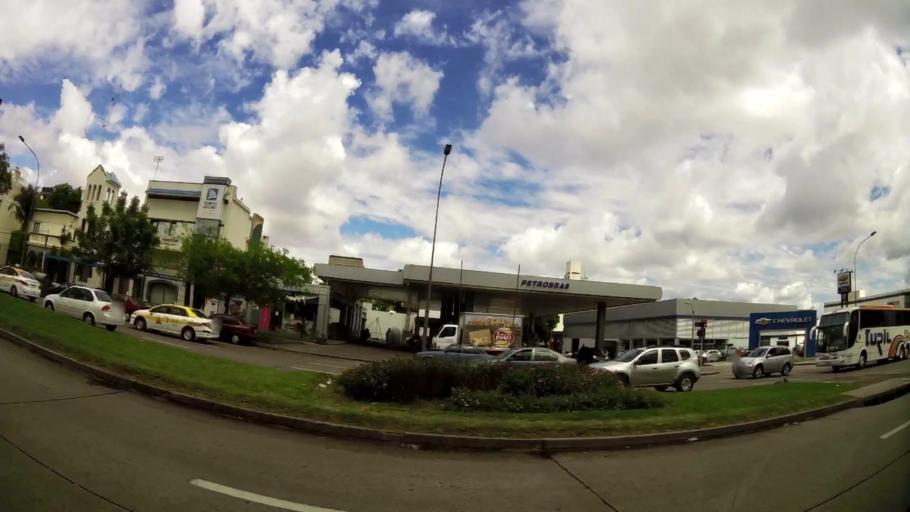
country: UY
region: Montevideo
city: Montevideo
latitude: -34.8899
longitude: -56.1658
